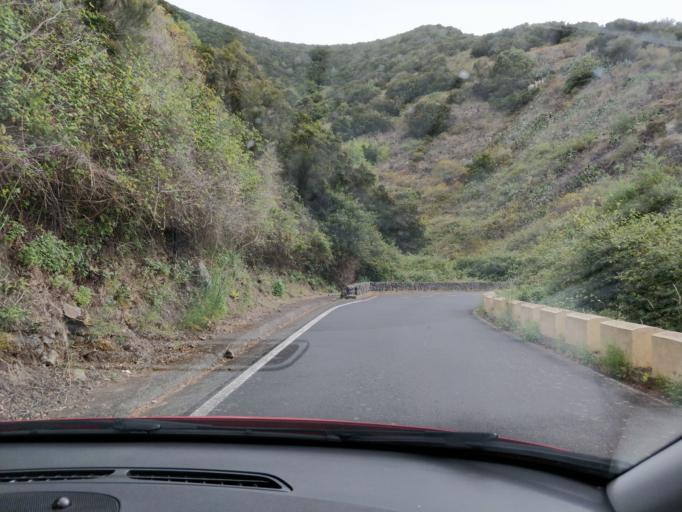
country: ES
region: Canary Islands
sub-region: Provincia de Santa Cruz de Tenerife
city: Santiago del Teide
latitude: 28.3221
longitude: -16.8461
